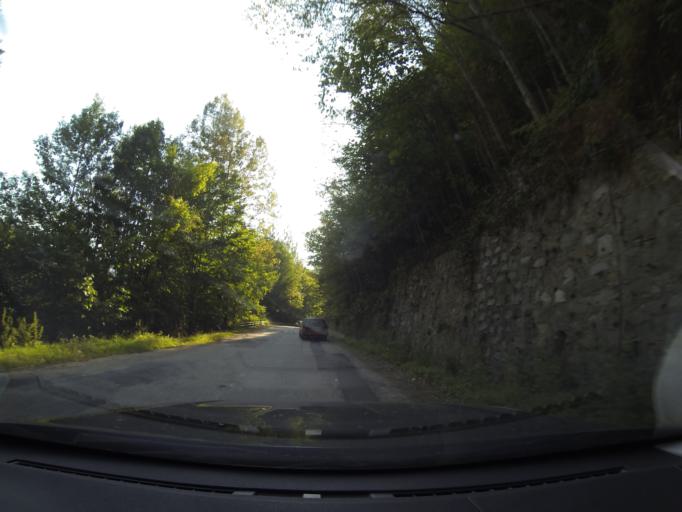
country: RO
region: Arges
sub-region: Comuna Arefu
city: Arefu
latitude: 45.3871
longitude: 24.6306
